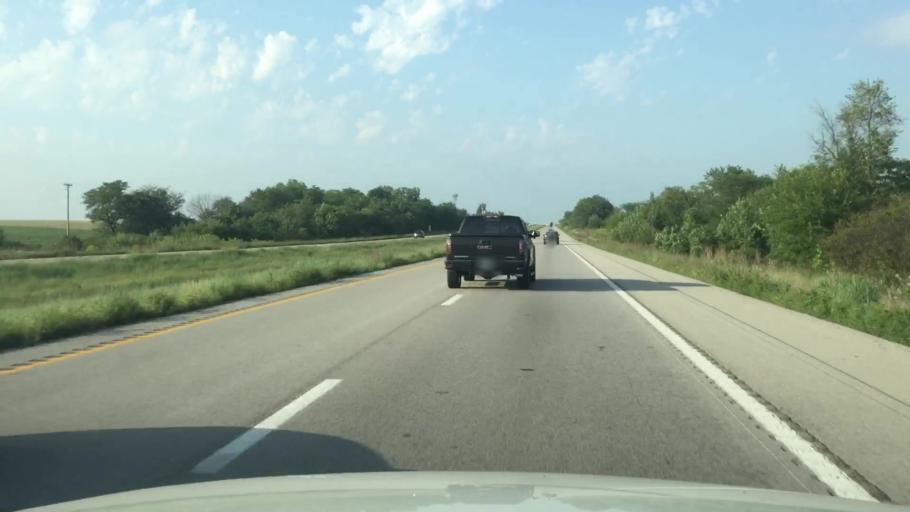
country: US
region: Missouri
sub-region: Clinton County
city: Cameron
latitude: 39.8199
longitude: -94.1915
